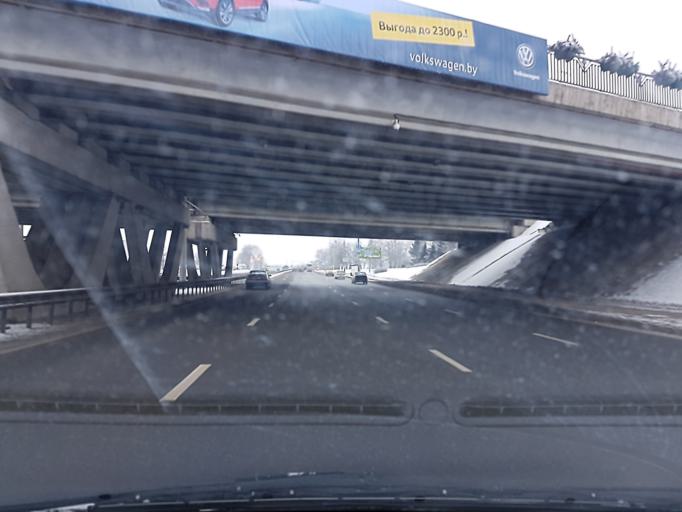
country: BY
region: Minsk
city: Shchomyslitsa
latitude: 53.8428
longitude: 27.4693
